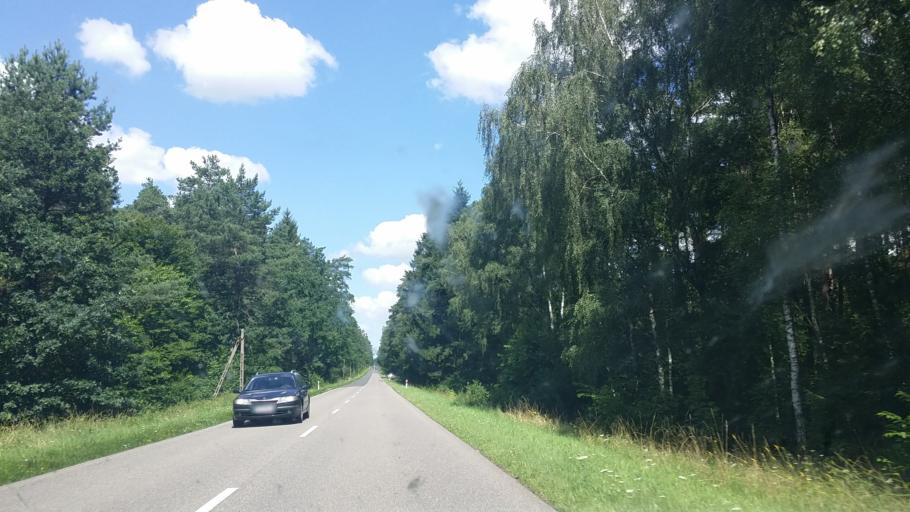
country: PL
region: West Pomeranian Voivodeship
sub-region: Powiat swidwinski
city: Slawoborze
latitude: 53.9347
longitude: 15.6783
